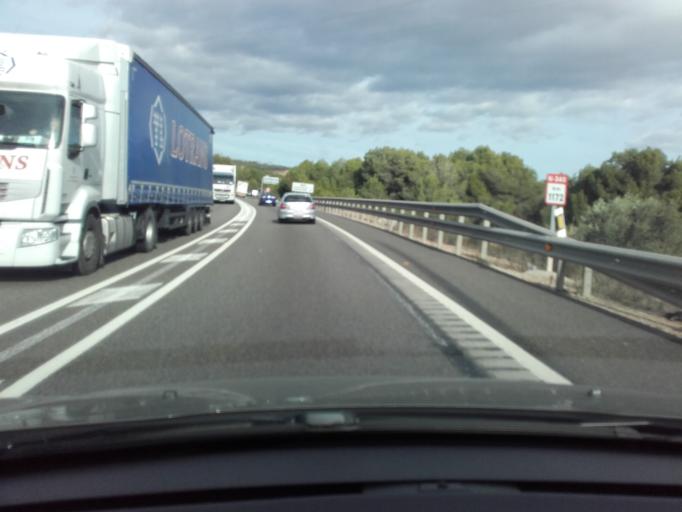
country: ES
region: Catalonia
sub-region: Provincia de Tarragona
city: Altafulla
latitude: 41.1415
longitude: 1.3506
